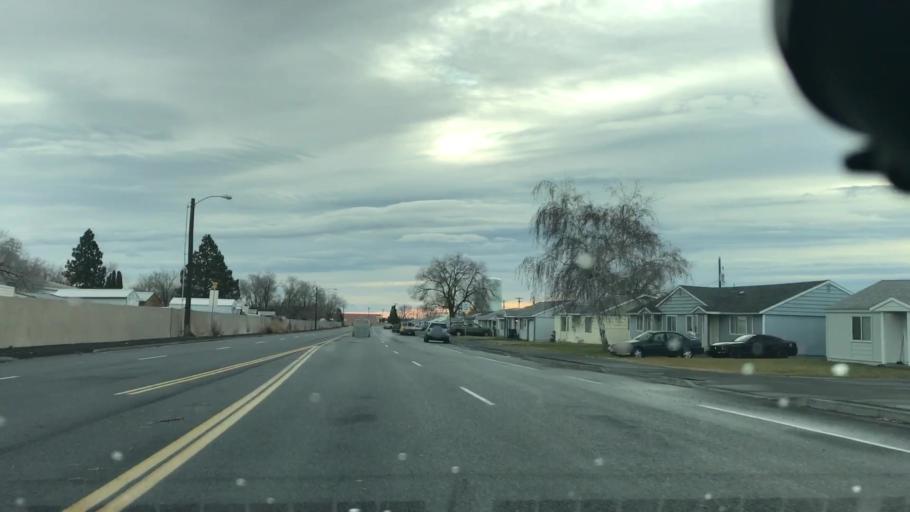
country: US
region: Washington
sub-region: Grant County
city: Moses Lake North
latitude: 47.1780
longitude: -119.3223
